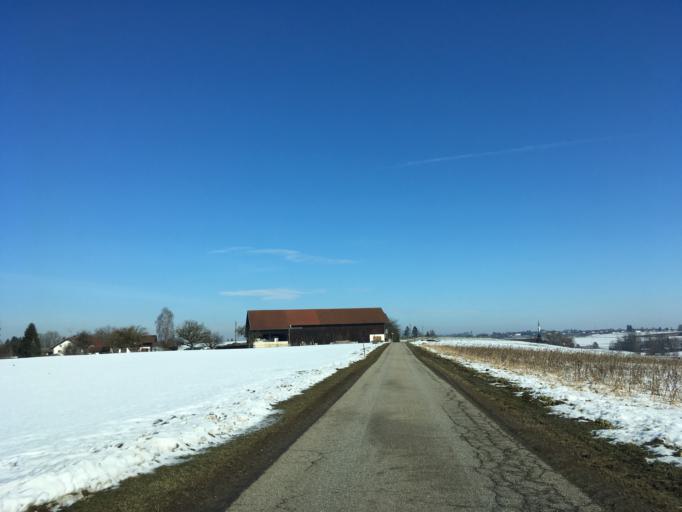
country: DE
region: Bavaria
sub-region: Upper Bavaria
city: Griesstatt
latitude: 47.9742
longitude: 12.1588
